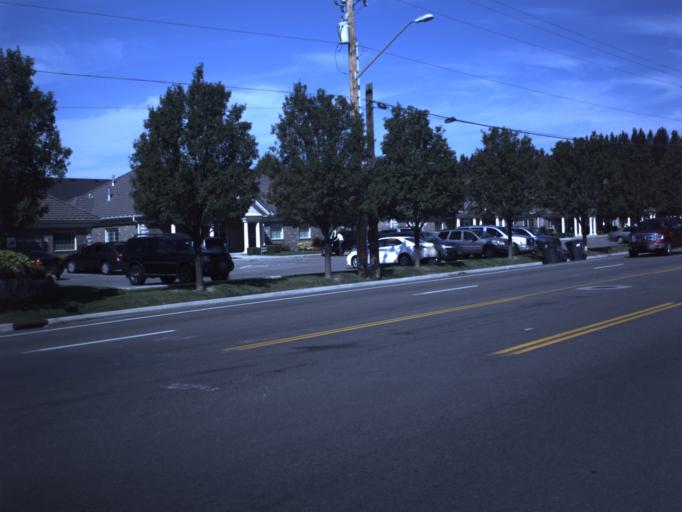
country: US
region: Utah
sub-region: Utah County
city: American Fork
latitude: 40.3723
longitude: -111.7691
